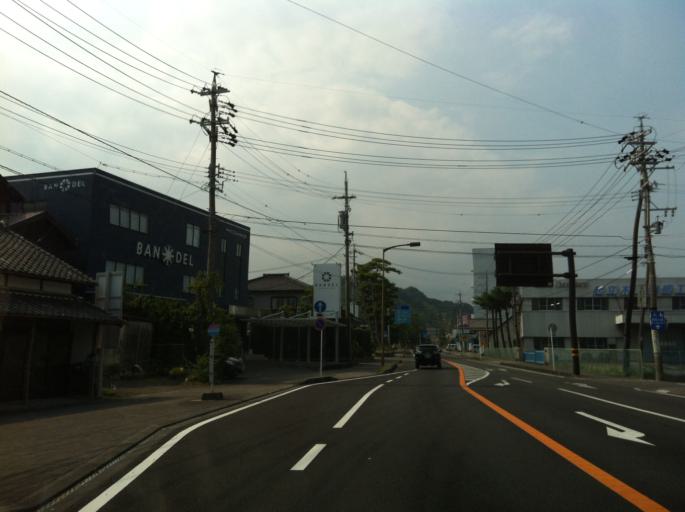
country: JP
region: Shizuoka
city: Fujieda
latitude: 34.9027
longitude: 138.2844
